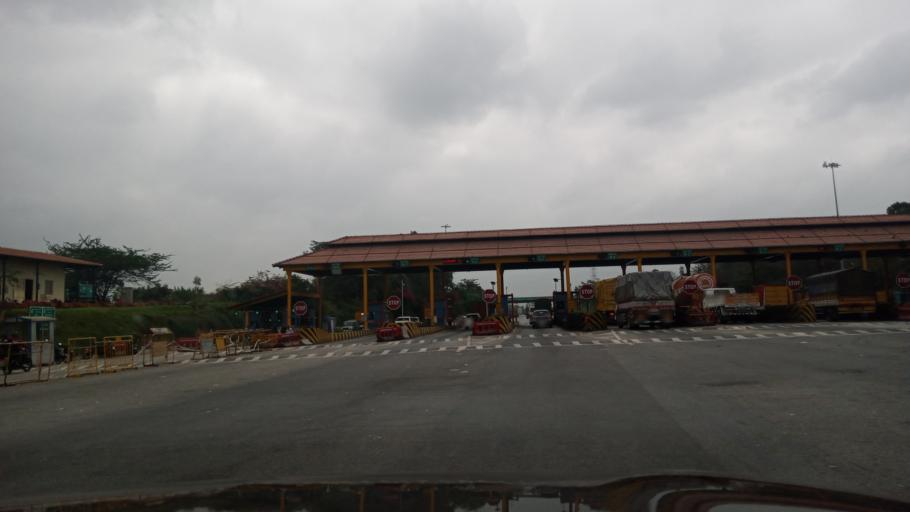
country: IN
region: Karnataka
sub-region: Bangalore Rural
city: Nelamangala
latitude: 13.0430
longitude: 77.4754
